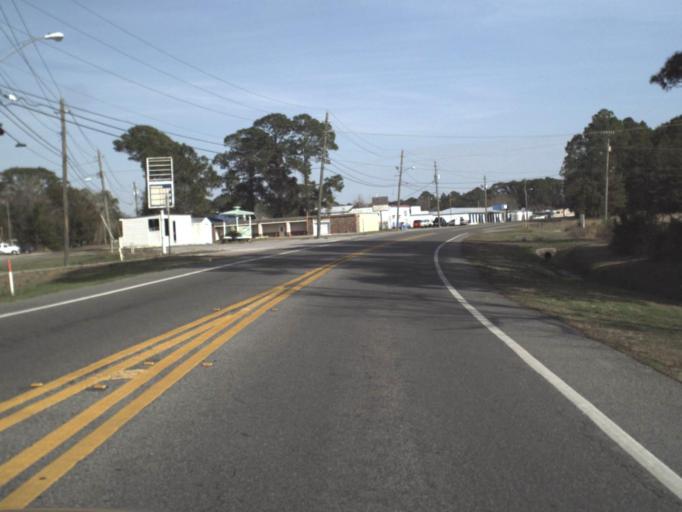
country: US
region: Florida
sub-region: Bay County
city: Parker
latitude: 30.1309
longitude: -85.5966
